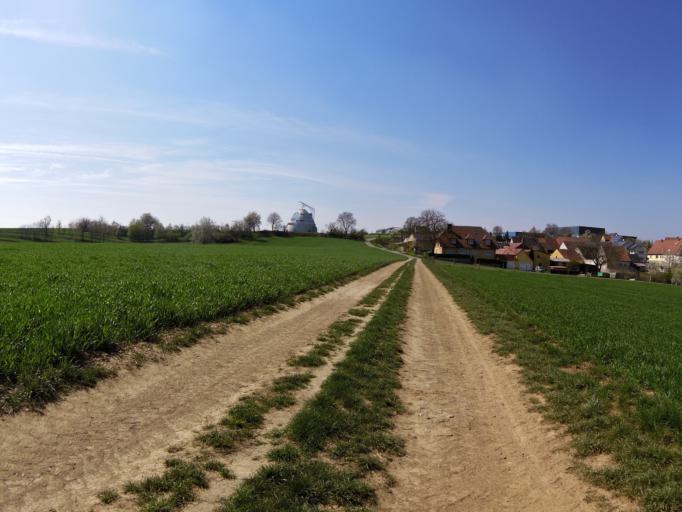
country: DE
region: Bavaria
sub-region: Regierungsbezirk Unterfranken
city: Biebelried
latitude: 49.7805
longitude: 10.0783
